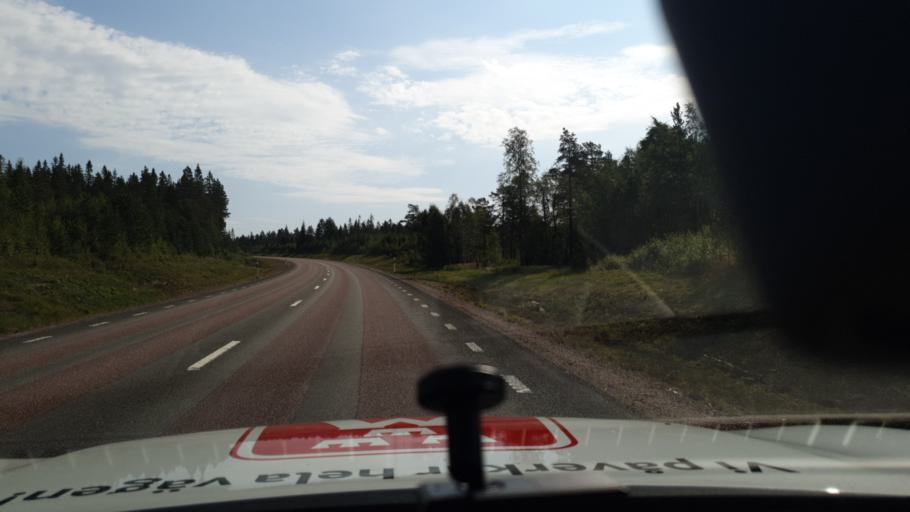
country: SE
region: Dalarna
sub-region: Malung-Saelens kommun
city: Malung
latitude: 60.5127
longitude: 13.4729
